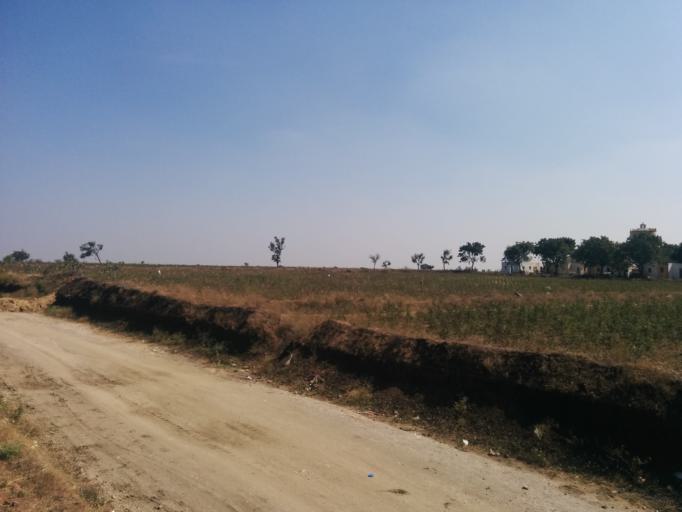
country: IN
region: Karnataka
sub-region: Gadag
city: Gadag
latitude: 15.4382
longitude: 75.6623
